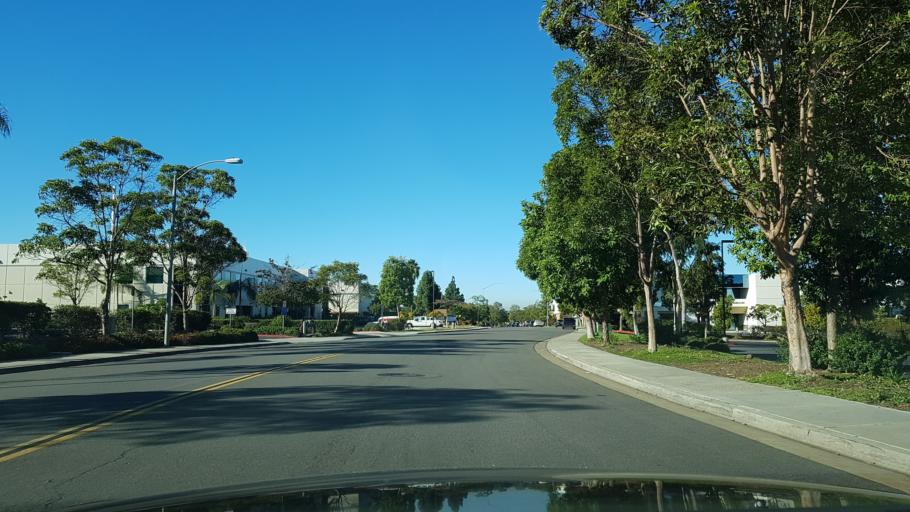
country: US
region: California
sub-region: San Diego County
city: Fairbanks Ranch
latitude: 32.9084
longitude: -117.1754
